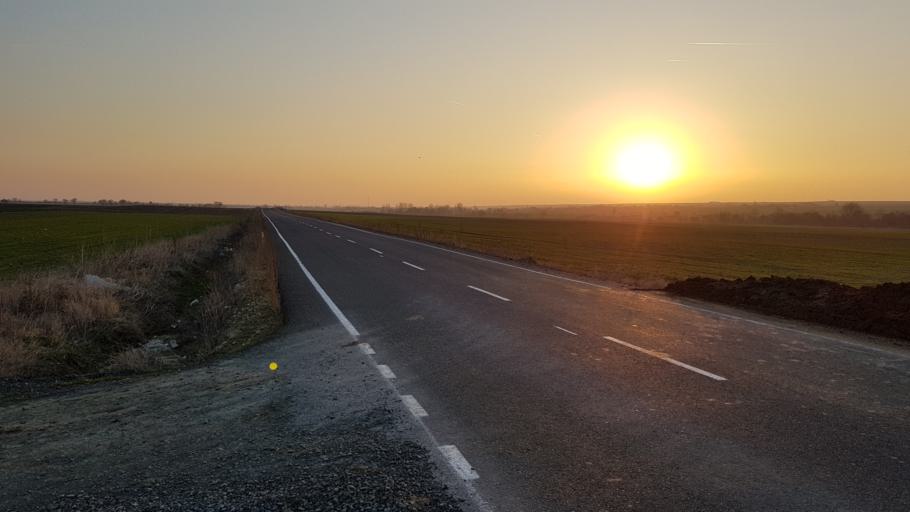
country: TR
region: Tekirdag
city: Velimese
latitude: 41.3211
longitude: 27.8147
